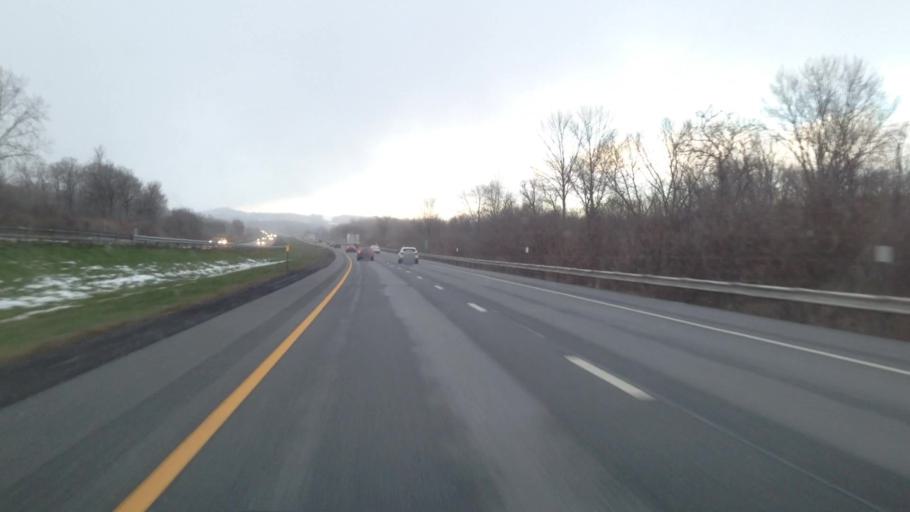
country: US
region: New York
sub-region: Montgomery County
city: Saint Johnsville
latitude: 42.9994
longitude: -74.7506
